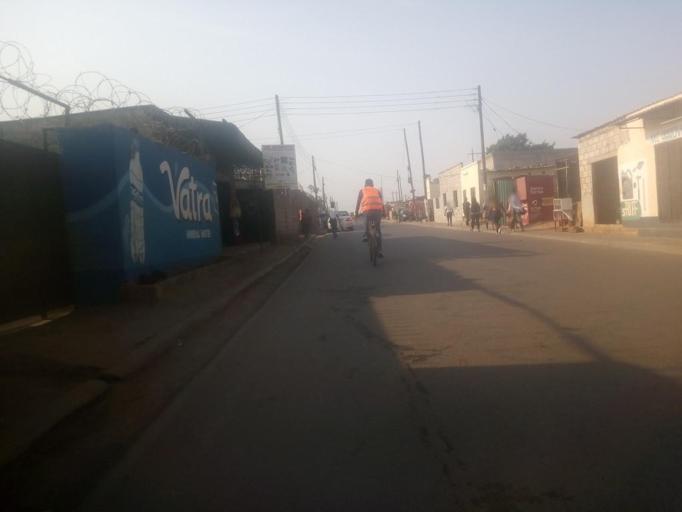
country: ZM
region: Lusaka
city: Lusaka
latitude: -15.4043
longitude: 28.3696
